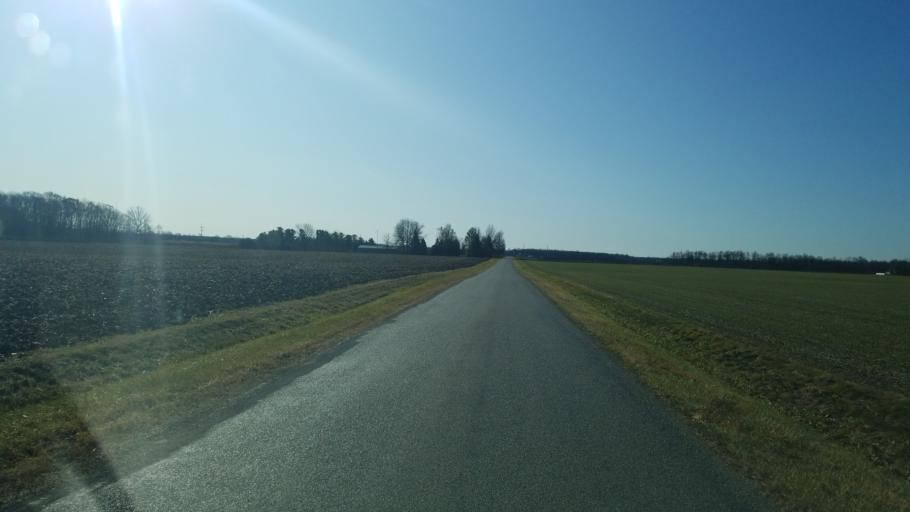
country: US
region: Ohio
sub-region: Crawford County
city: Crestline
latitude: 40.8329
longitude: -82.7060
